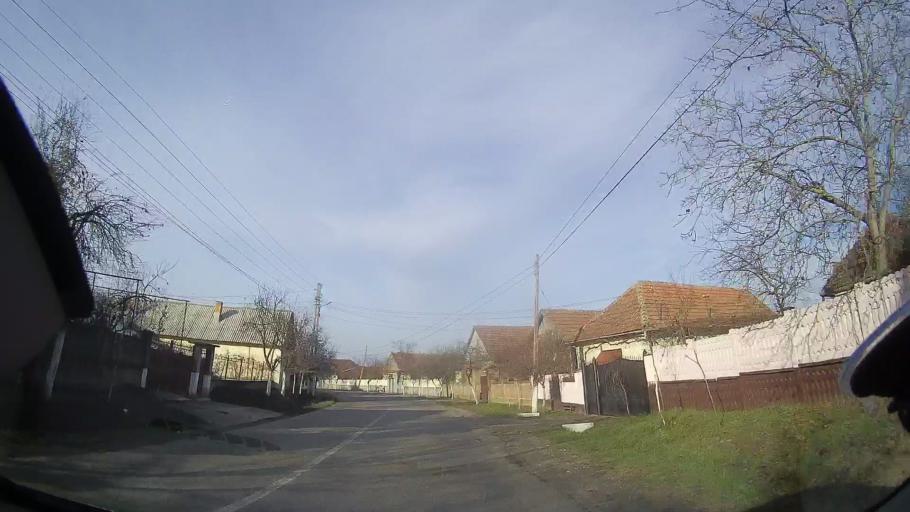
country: RO
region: Bihor
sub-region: Comuna Spinus
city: Spinus
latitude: 47.1781
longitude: 22.2179
